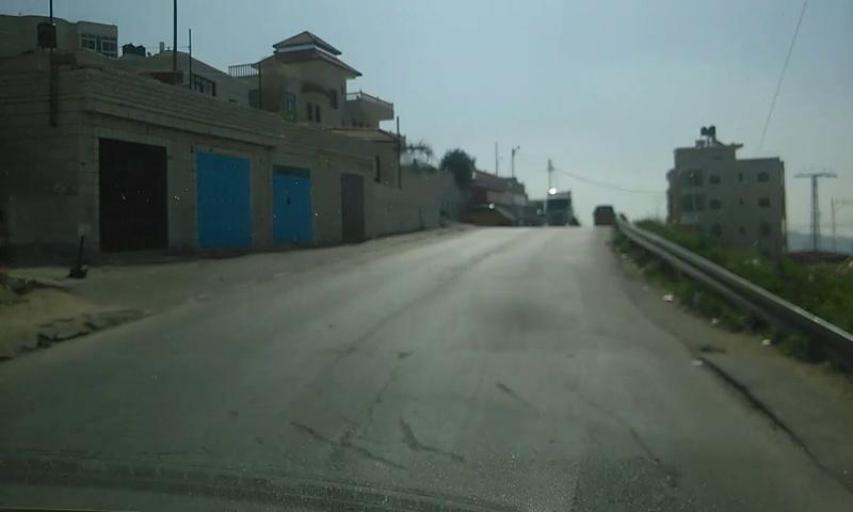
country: PS
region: West Bank
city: Dayr Jarir
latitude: 31.9684
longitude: 35.2900
